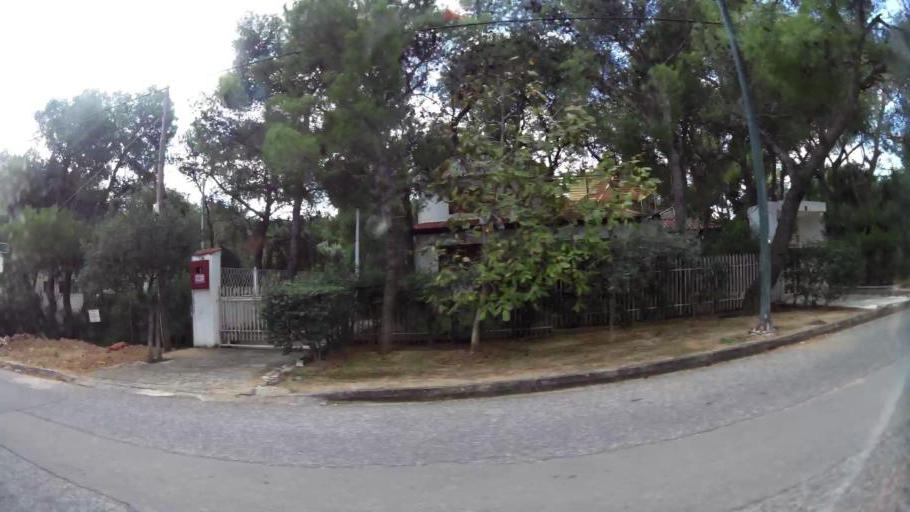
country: GR
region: Attica
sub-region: Nomarchia Anatolikis Attikis
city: Thrakomakedones
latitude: 38.1301
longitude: 23.7613
